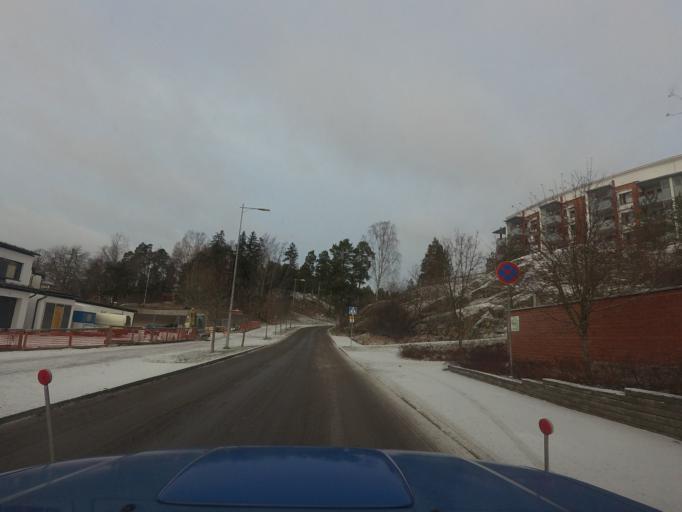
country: FI
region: Uusimaa
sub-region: Helsinki
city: Espoo
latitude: 60.1622
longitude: 24.6133
